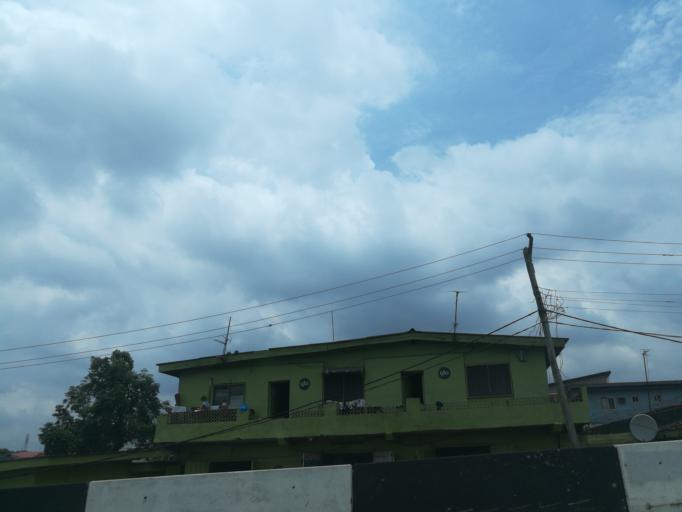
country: NG
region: Lagos
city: Ojota
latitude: 6.5965
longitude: 3.3658
